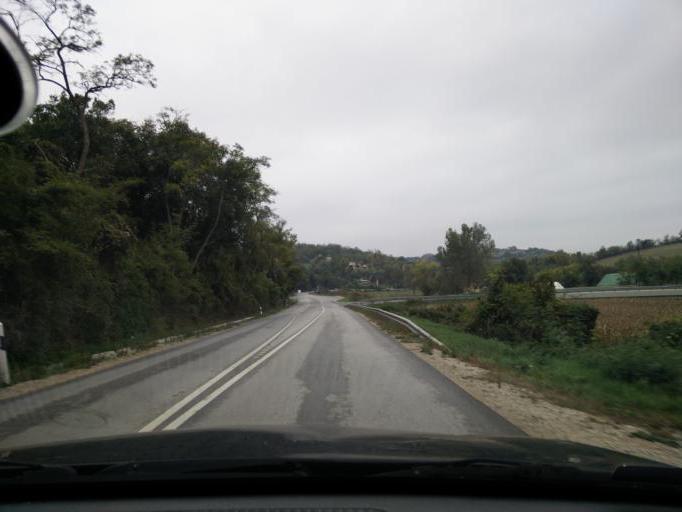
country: HU
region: Komarom-Esztergom
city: Tokod
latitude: 47.7113
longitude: 18.6275
